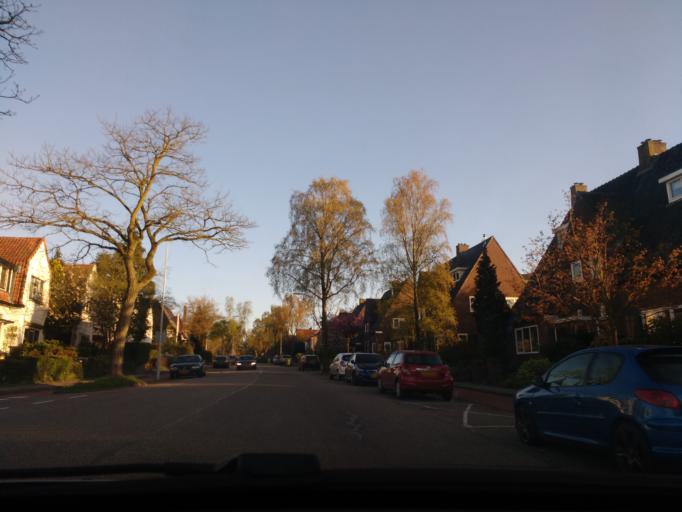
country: NL
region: Gelderland
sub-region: Gemeente Wageningen
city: Wageningen
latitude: 51.9706
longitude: 5.6828
